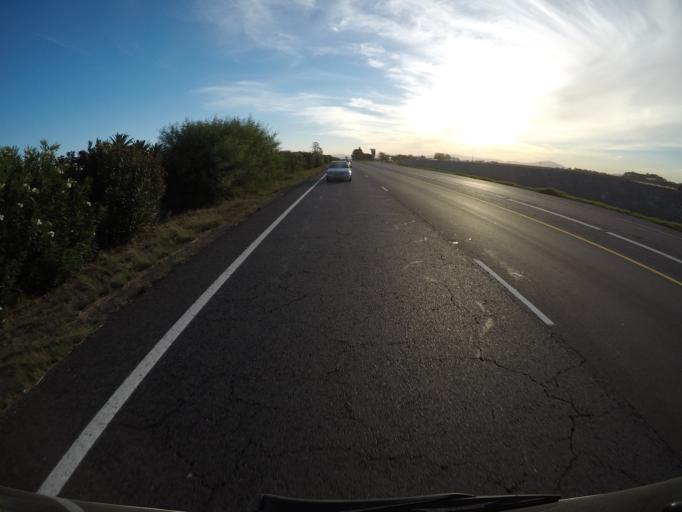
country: ZA
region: Western Cape
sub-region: City of Cape Town
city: Kraaifontein
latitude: -33.8265
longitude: 18.7675
